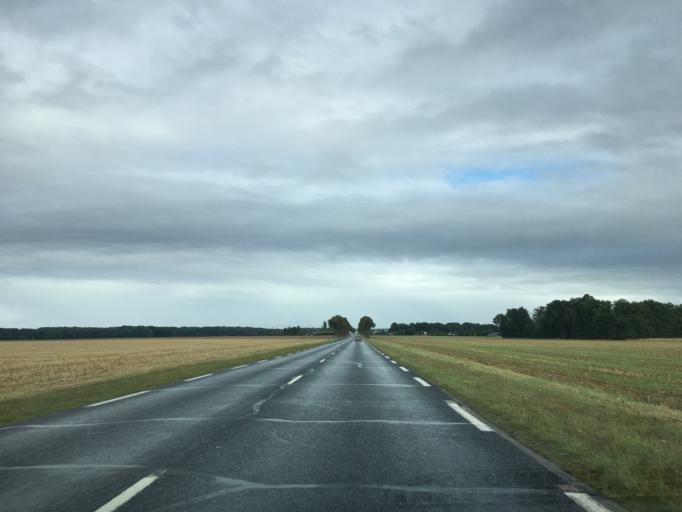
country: FR
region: Haute-Normandie
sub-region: Departement de l'Eure
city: Francheville
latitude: 48.7435
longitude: 0.8509
